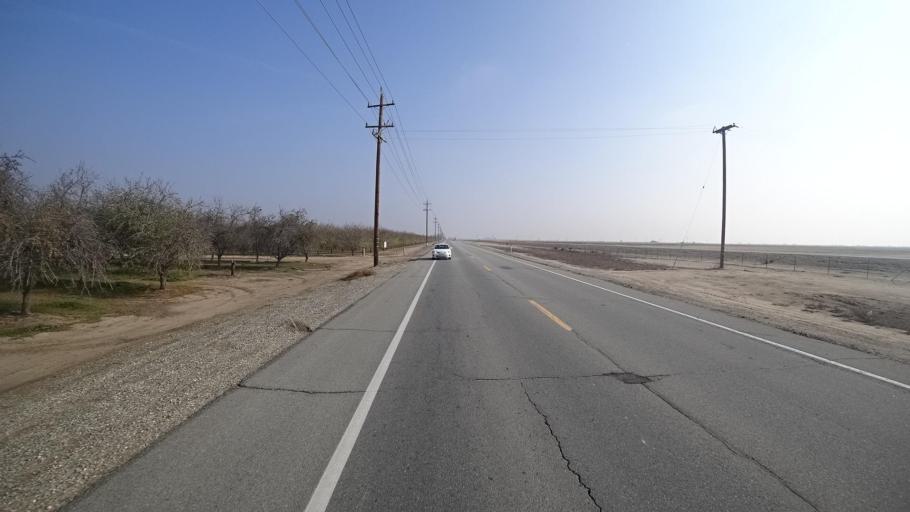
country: US
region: California
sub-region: Kern County
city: Rosedale
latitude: 35.3545
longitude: -119.2614
